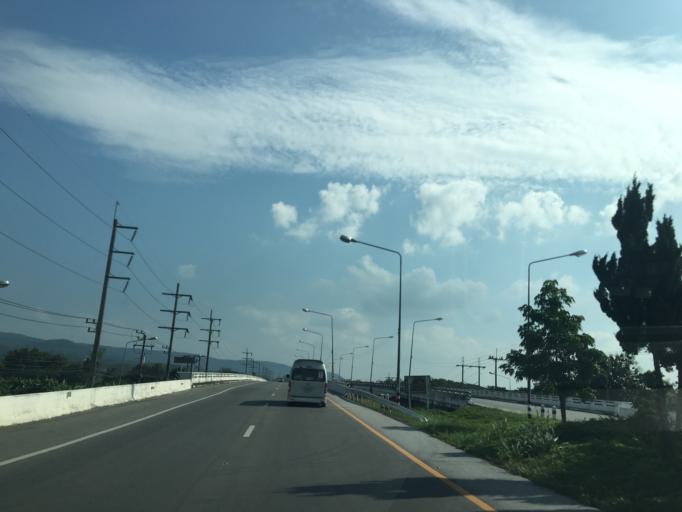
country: TH
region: Chiang Rai
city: Mae Lao
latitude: 19.7166
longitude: 99.7168
